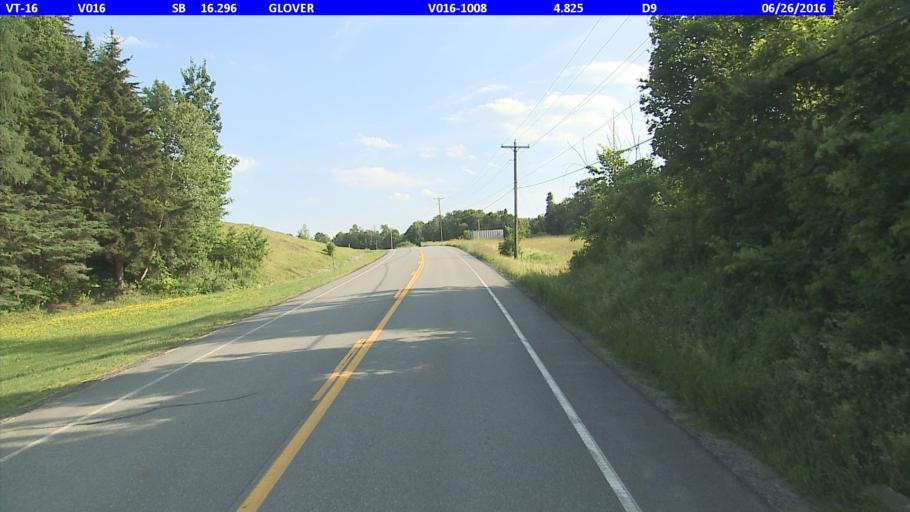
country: US
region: Vermont
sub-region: Orleans County
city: Newport
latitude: 44.6913
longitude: -72.1926
